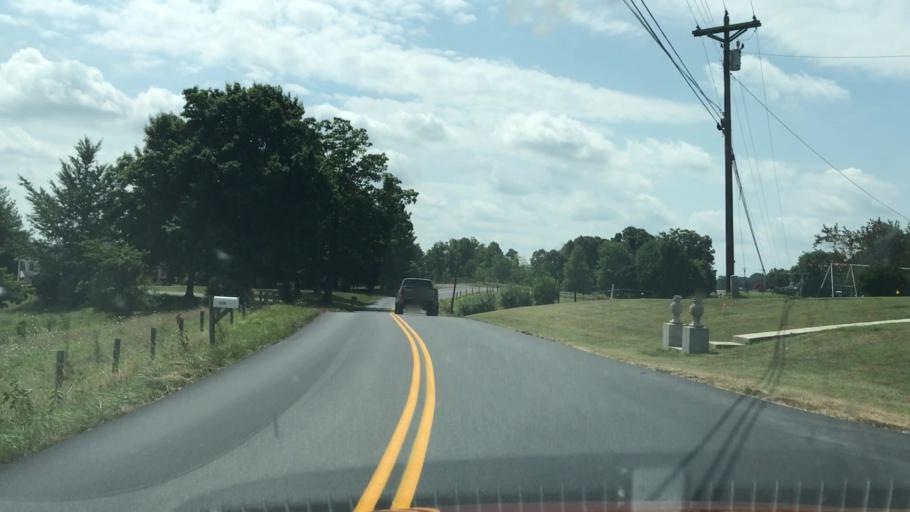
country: US
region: Kentucky
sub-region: Monroe County
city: Tompkinsville
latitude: 36.7253
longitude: -85.7222
